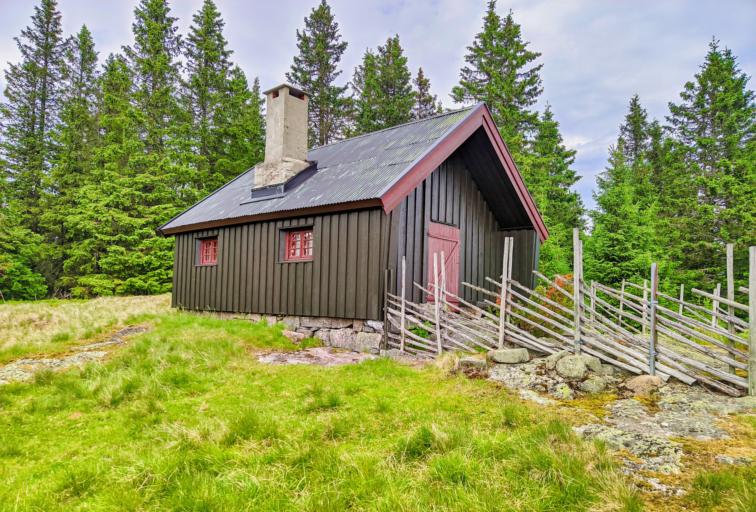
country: NO
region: Akershus
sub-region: Hurdal
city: Hurdal
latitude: 60.5622
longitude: 11.1132
